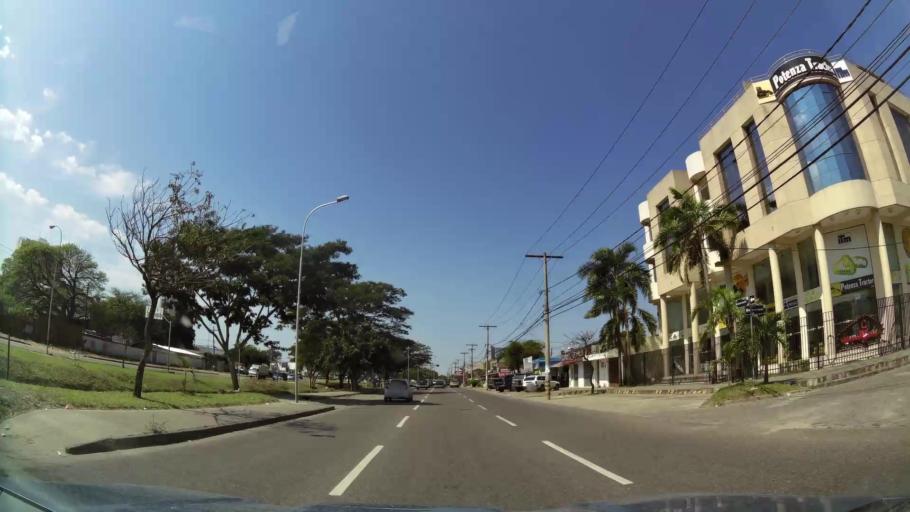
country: BO
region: Santa Cruz
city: Santa Cruz de la Sierra
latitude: -17.7507
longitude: -63.1710
